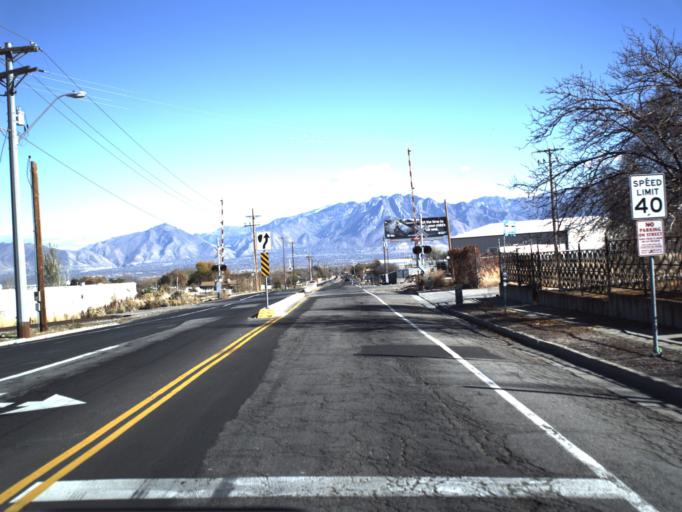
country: US
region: Utah
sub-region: Salt Lake County
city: Kearns
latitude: 40.6675
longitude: -112.0245
